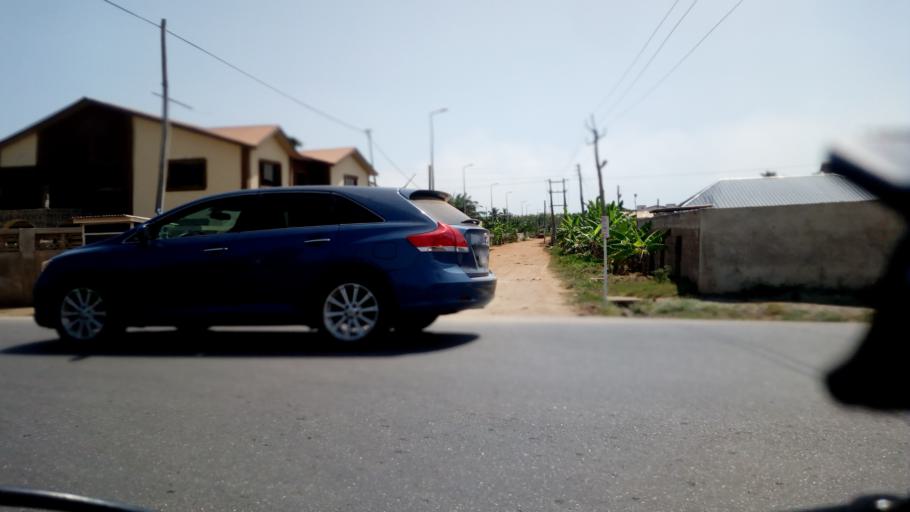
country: GH
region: Central
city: Cape Coast
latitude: 5.1344
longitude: -1.2788
